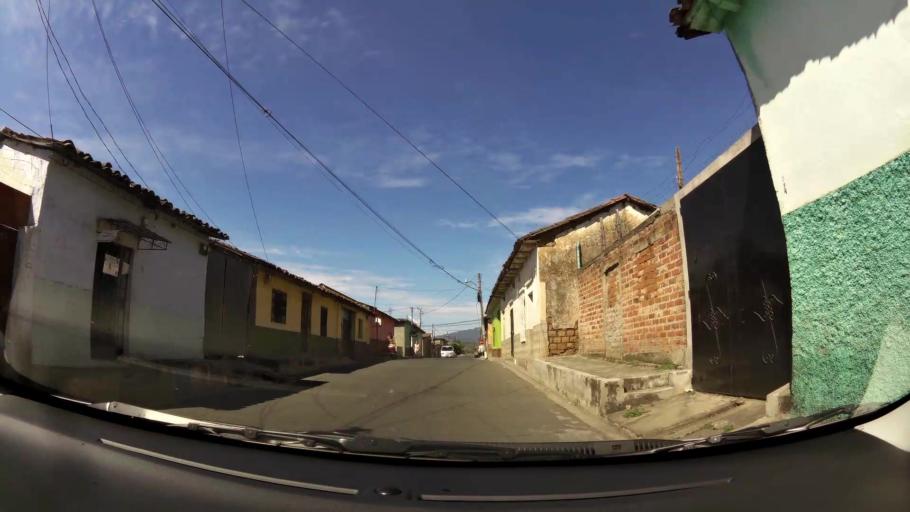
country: SV
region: Santa Ana
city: Chalchuapa
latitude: 13.9867
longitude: -89.6816
